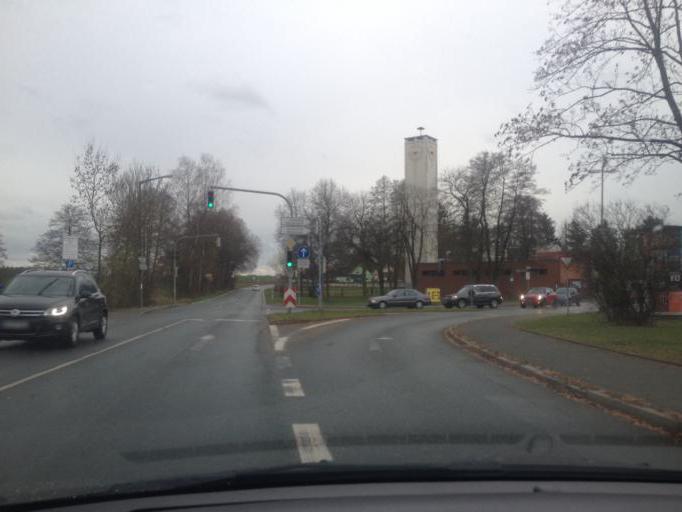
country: DE
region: Bavaria
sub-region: Regierungsbezirk Mittelfranken
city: Wendelstein
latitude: 49.3730
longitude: 11.0995
